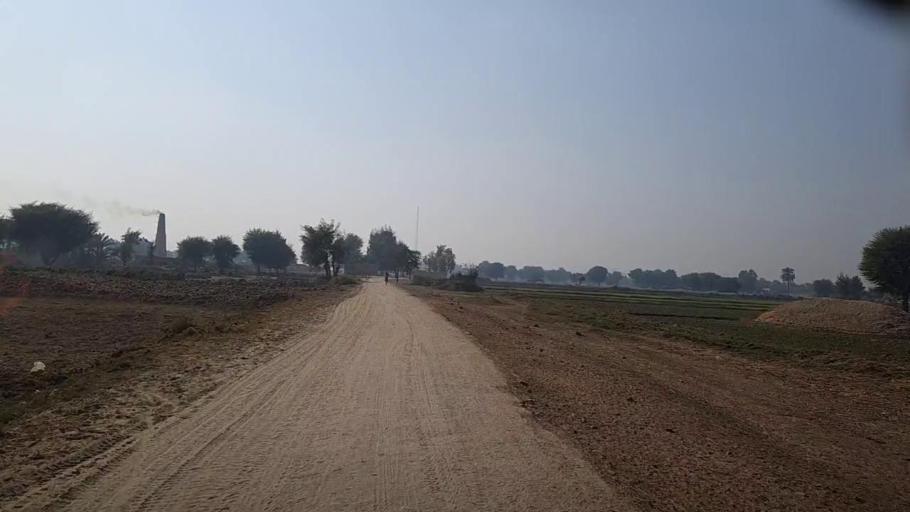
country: PK
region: Sindh
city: Bozdar
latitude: 27.2132
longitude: 68.5770
